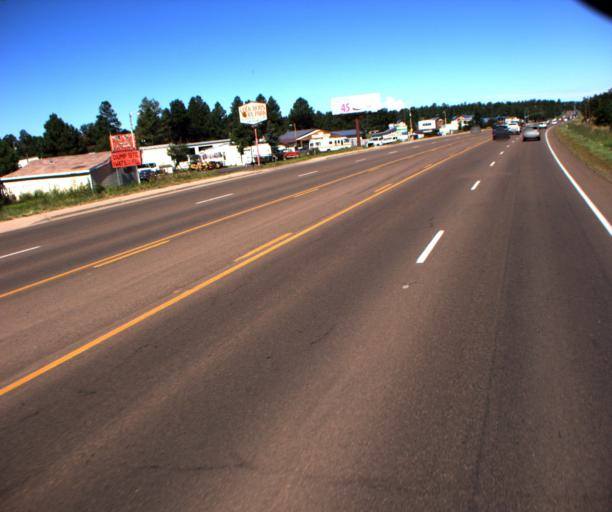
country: US
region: Arizona
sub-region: Navajo County
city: Lake of the Woods
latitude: 34.1702
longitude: -110.0008
